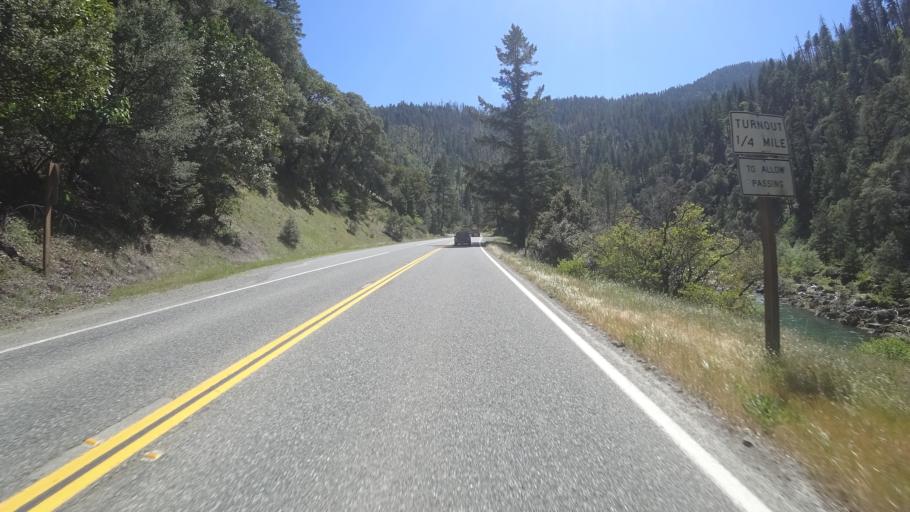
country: US
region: California
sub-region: Trinity County
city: Hayfork
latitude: 40.7692
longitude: -123.3068
